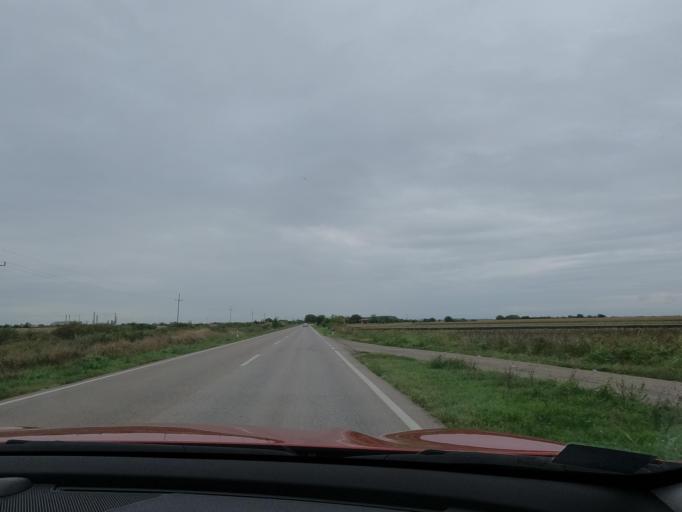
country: RS
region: Autonomna Pokrajina Vojvodina
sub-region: Severnobanatski Okrug
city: Kikinda
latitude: 45.7759
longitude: 20.4274
